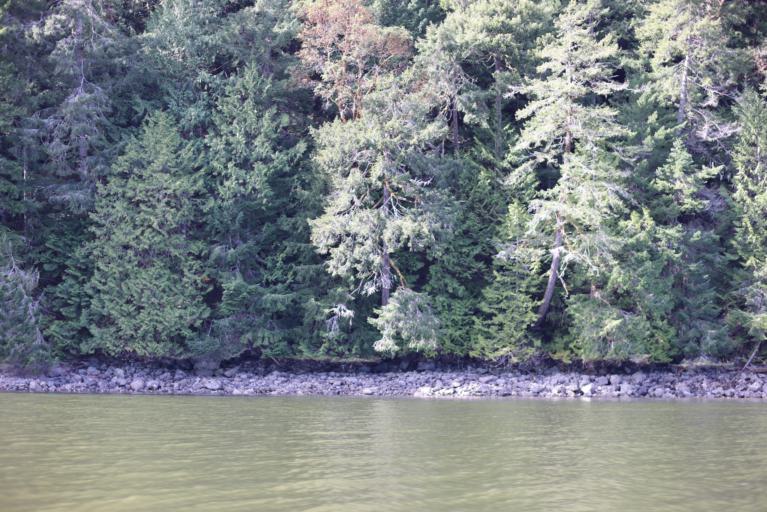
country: CA
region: British Columbia
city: Langford
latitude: 48.5307
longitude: -123.5486
